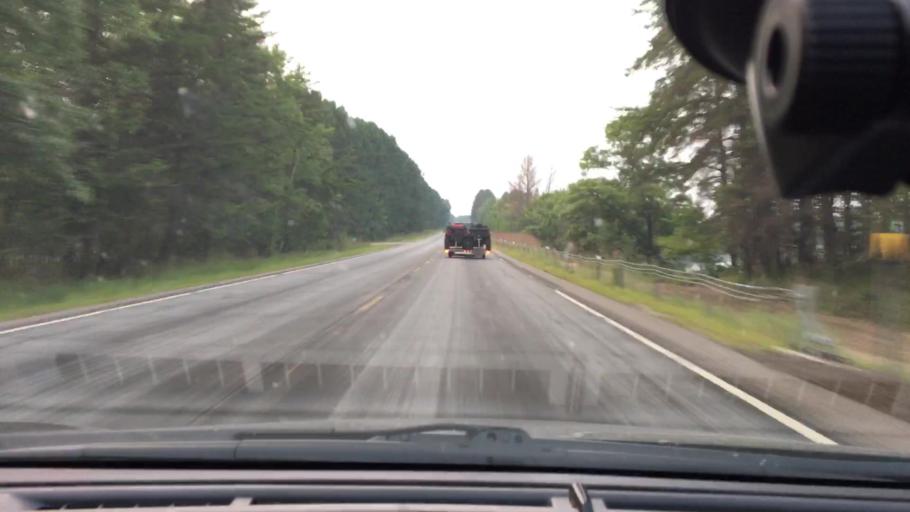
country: US
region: Minnesota
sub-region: Crow Wing County
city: Cross Lake
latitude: 46.7821
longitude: -93.9663
